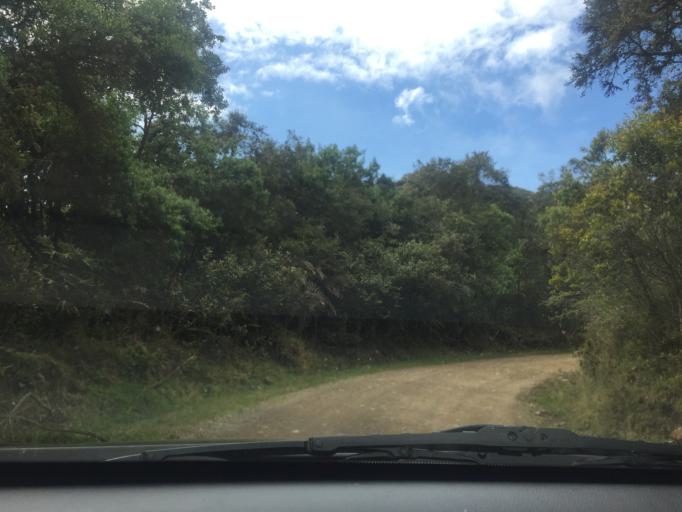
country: CO
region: Cundinamarca
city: Facatativa
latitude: 4.7925
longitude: -74.3808
